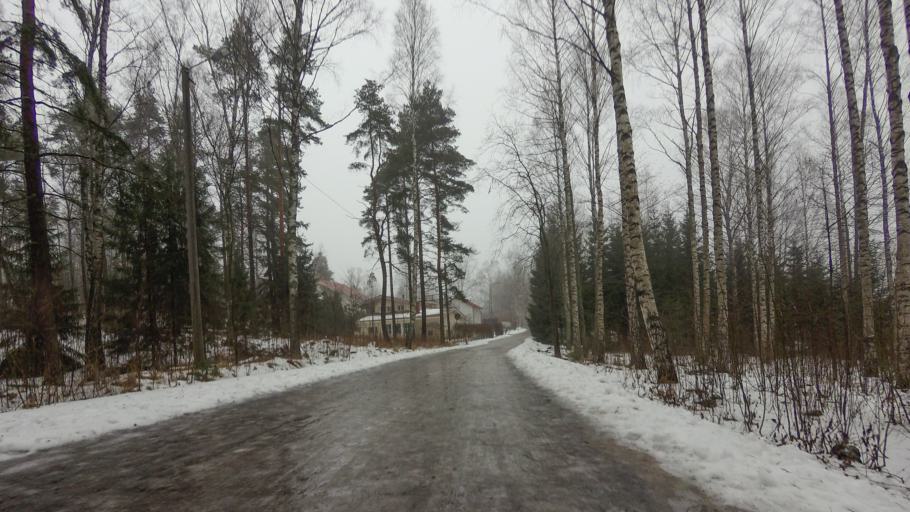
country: FI
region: Uusimaa
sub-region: Helsinki
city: Vantaa
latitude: 60.2123
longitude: 25.0459
